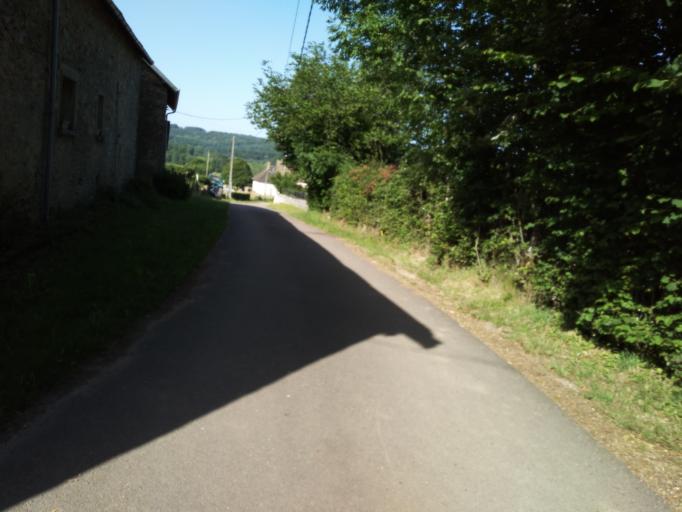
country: FR
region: Bourgogne
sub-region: Departement de la Cote-d'Or
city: Saulieu
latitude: 47.2887
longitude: 4.1389
